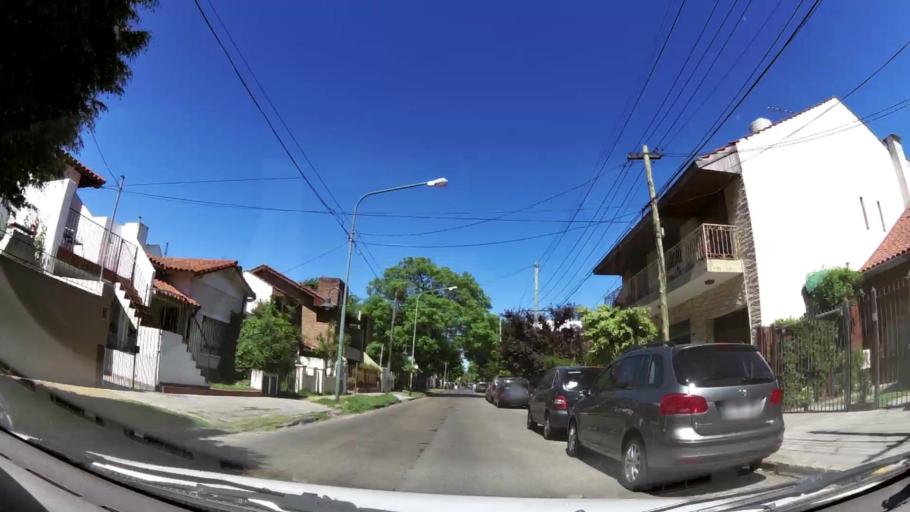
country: AR
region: Buenos Aires
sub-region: Partido de Vicente Lopez
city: Olivos
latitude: -34.5221
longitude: -58.5007
